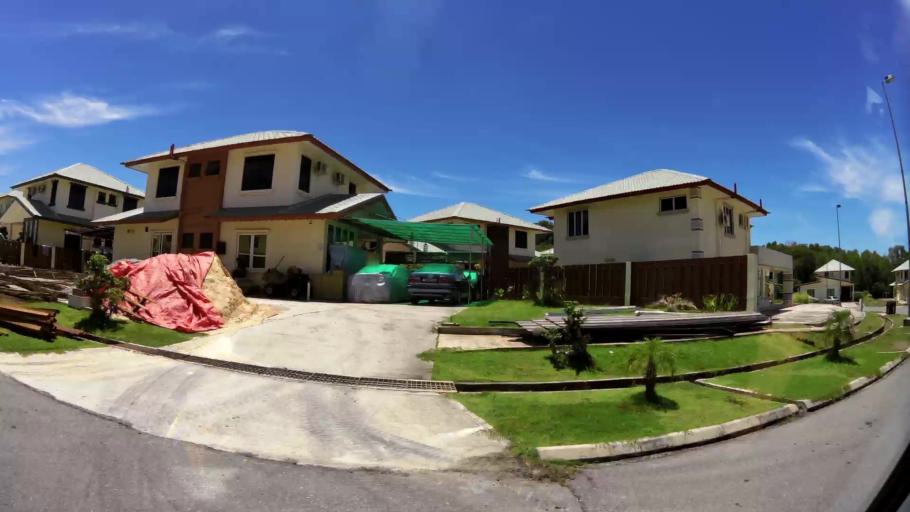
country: BN
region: Brunei and Muara
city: Bandar Seri Begawan
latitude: 5.0327
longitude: 115.0407
